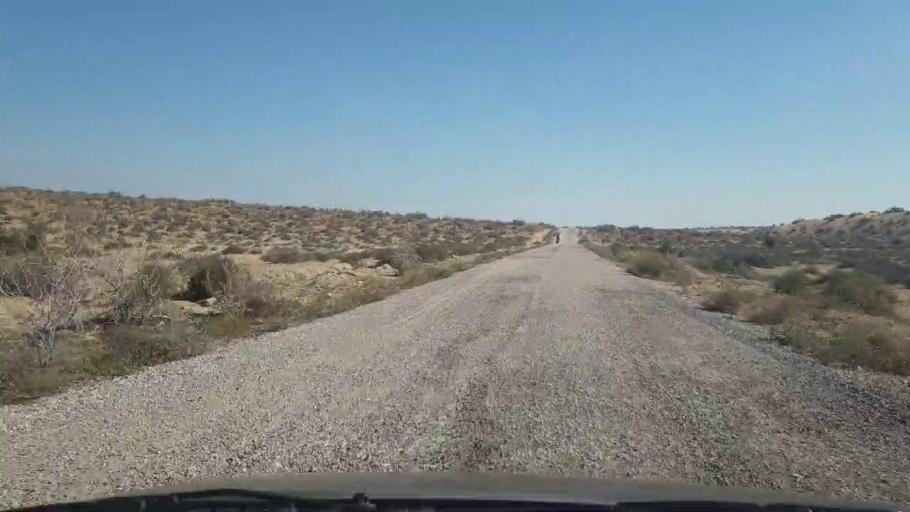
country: PK
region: Sindh
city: Bozdar
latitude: 27.0005
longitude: 68.8498
